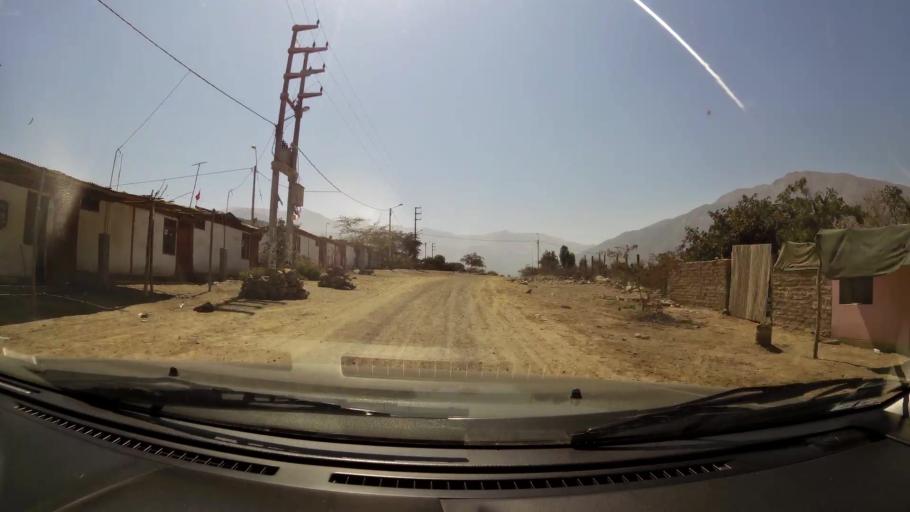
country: PE
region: Ica
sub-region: Provincia de Ica
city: Guadalupe
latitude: -13.8754
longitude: -75.6424
